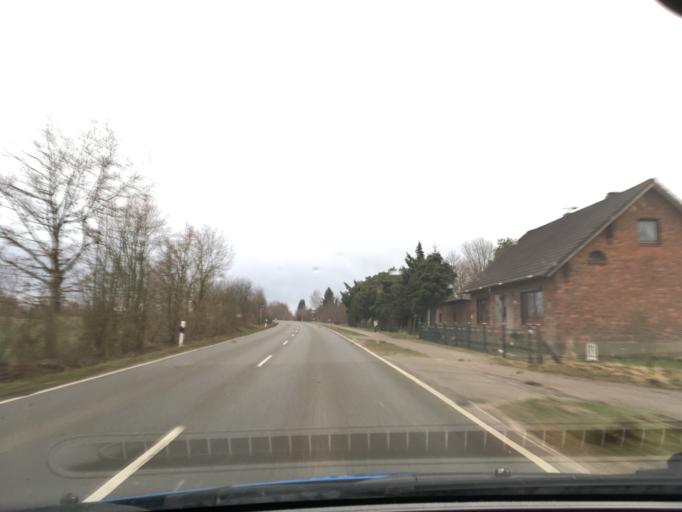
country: DE
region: Schleswig-Holstein
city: Siebeneichen
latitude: 53.5018
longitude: 10.6134
